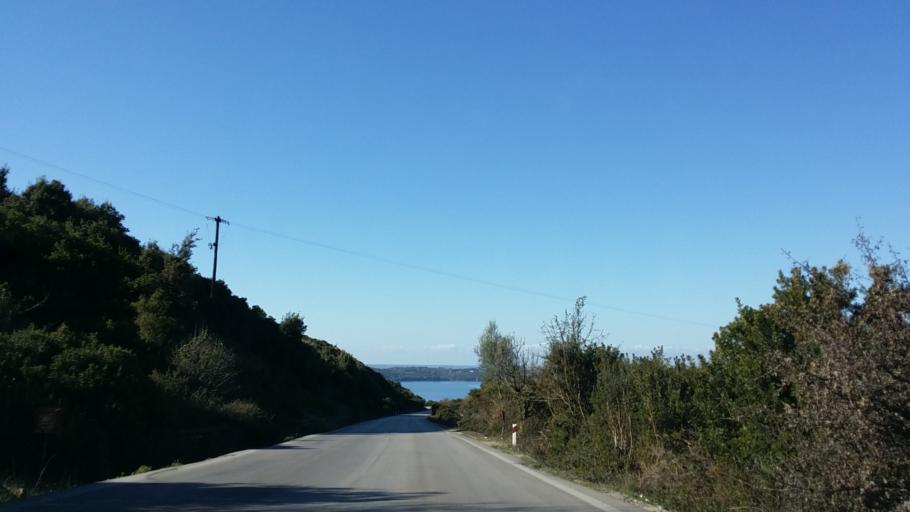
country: GR
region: West Greece
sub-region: Nomos Aitolias kai Akarnanias
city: Vonitsa
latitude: 38.9289
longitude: 20.9212
